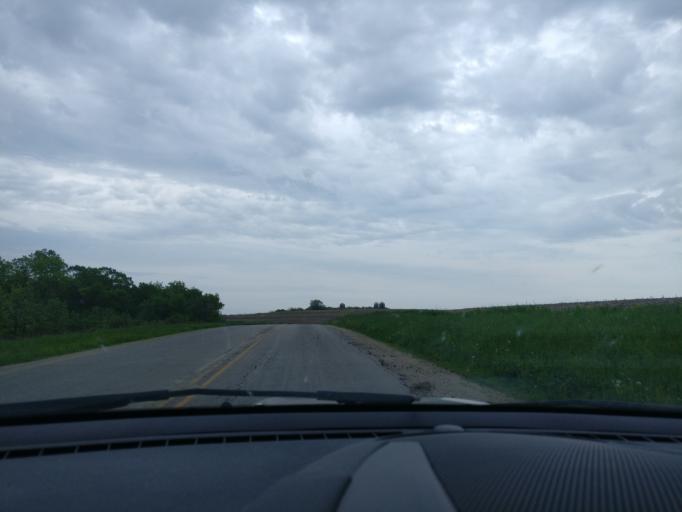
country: US
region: Wisconsin
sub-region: Lafayette County
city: Darlington
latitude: 42.7507
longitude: -89.9983
